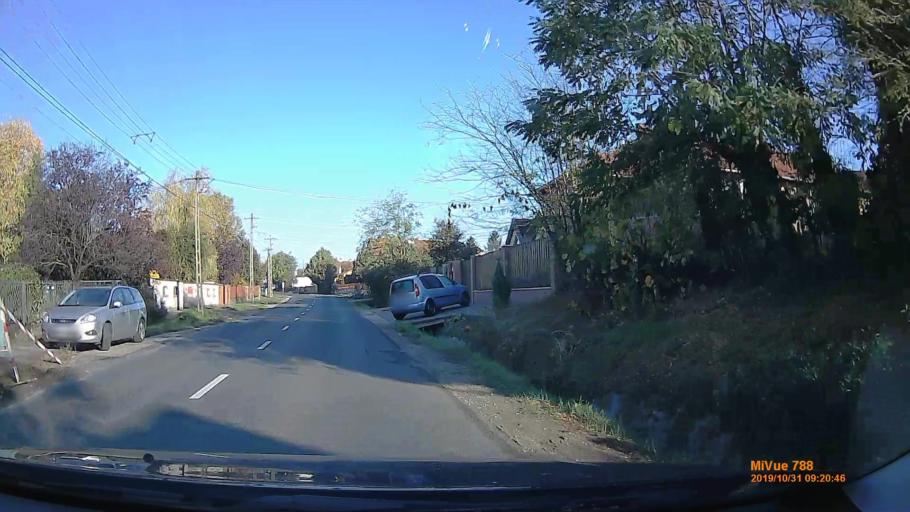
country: HU
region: Pest
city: Gyomro
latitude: 47.4260
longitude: 19.3838
